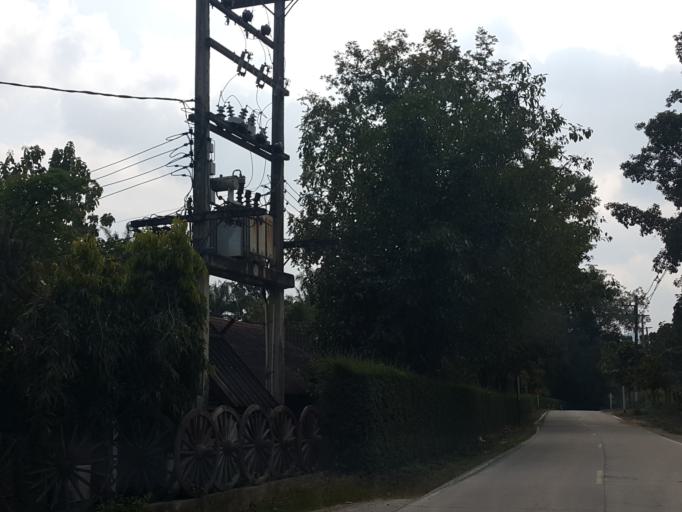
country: TH
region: Chiang Mai
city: Mae On
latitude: 18.8190
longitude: 99.2236
